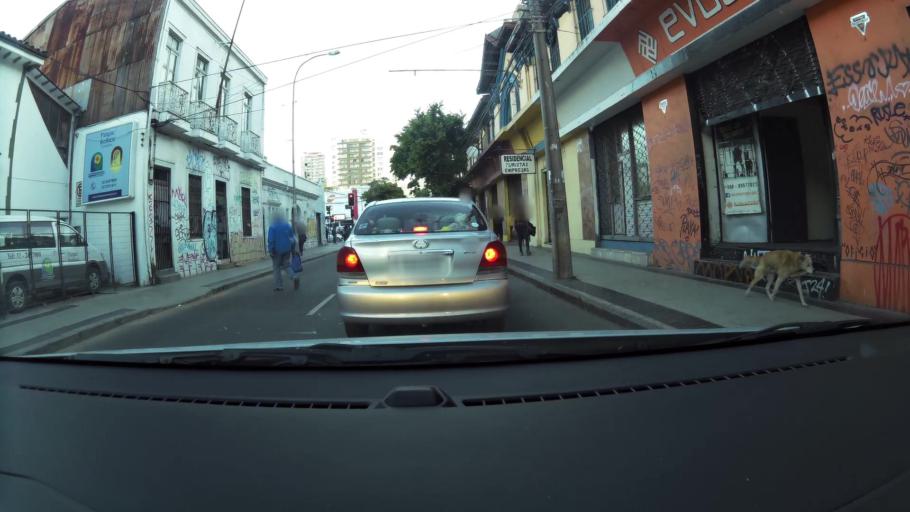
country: CL
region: Valparaiso
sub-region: Provincia de Valparaiso
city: Vina del Mar
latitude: -33.0222
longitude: -71.5610
